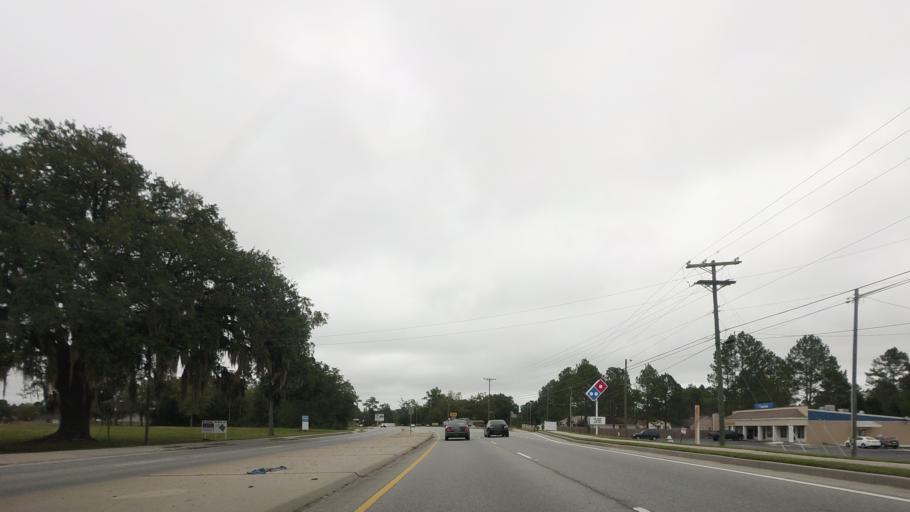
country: US
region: Georgia
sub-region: Lowndes County
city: Valdosta
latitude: 30.9287
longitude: -83.2449
